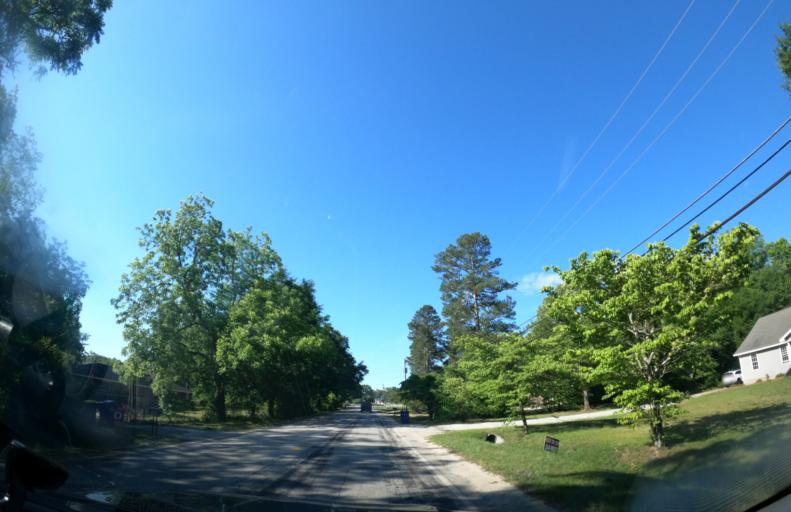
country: US
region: Georgia
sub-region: Columbia County
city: Harlem
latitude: 33.4073
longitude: -82.3145
